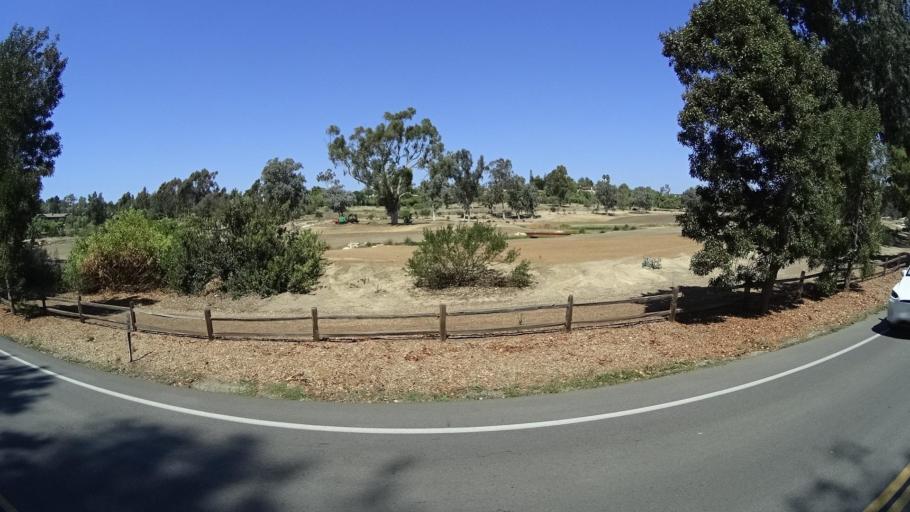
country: US
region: California
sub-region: San Diego County
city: Rancho Santa Fe
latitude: 33.0219
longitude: -117.2246
